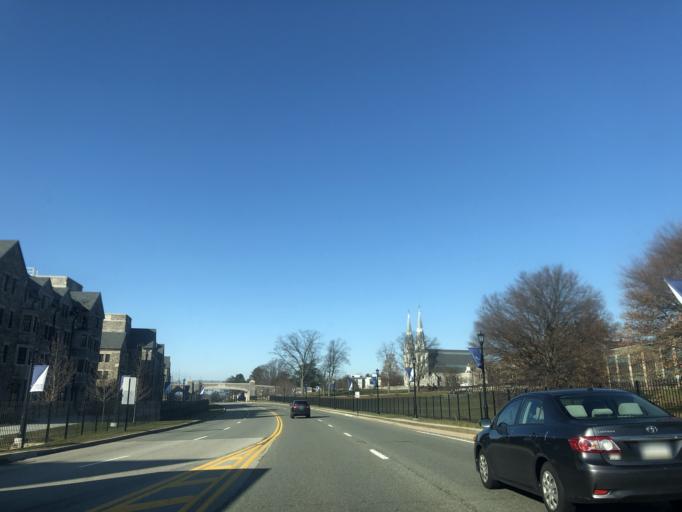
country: US
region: Pennsylvania
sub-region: Delaware County
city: Radnor
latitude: 40.0342
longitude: -75.3404
